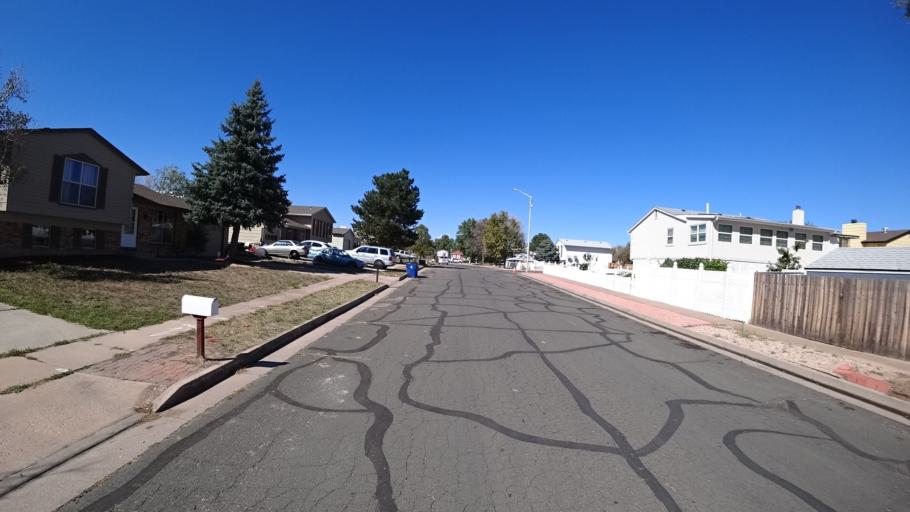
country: US
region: Colorado
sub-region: El Paso County
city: Stratmoor
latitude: 38.7910
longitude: -104.7365
